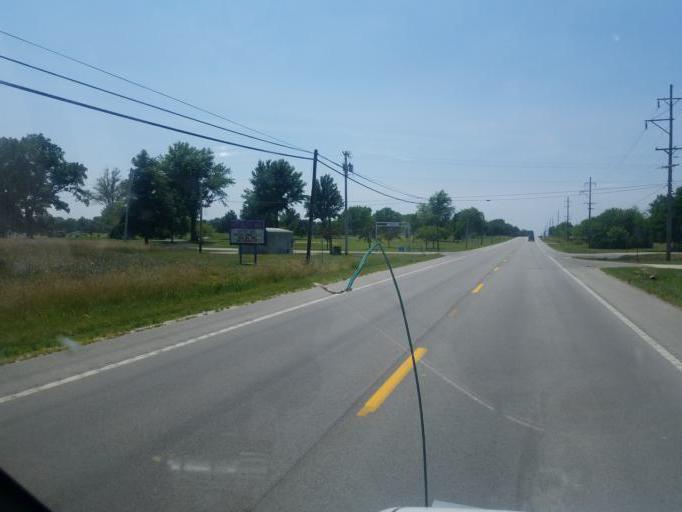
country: US
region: Ohio
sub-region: Auglaize County
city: Saint Marys
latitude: 40.5511
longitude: -84.4738
